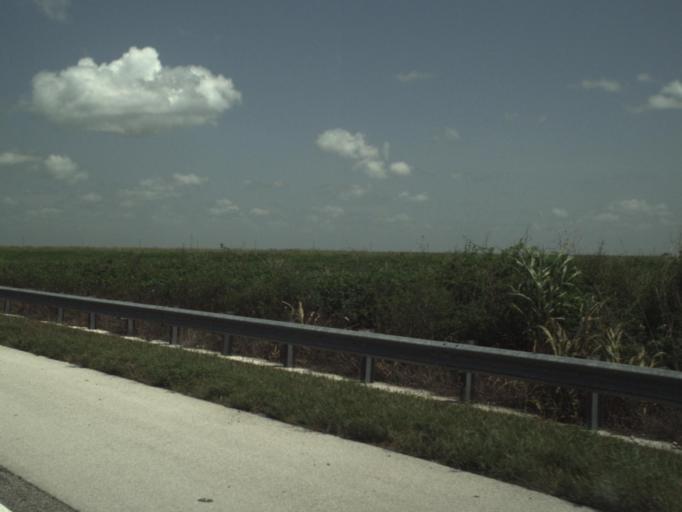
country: US
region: Florida
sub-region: Palm Beach County
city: Belle Glade Camp
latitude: 26.3952
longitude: -80.5843
